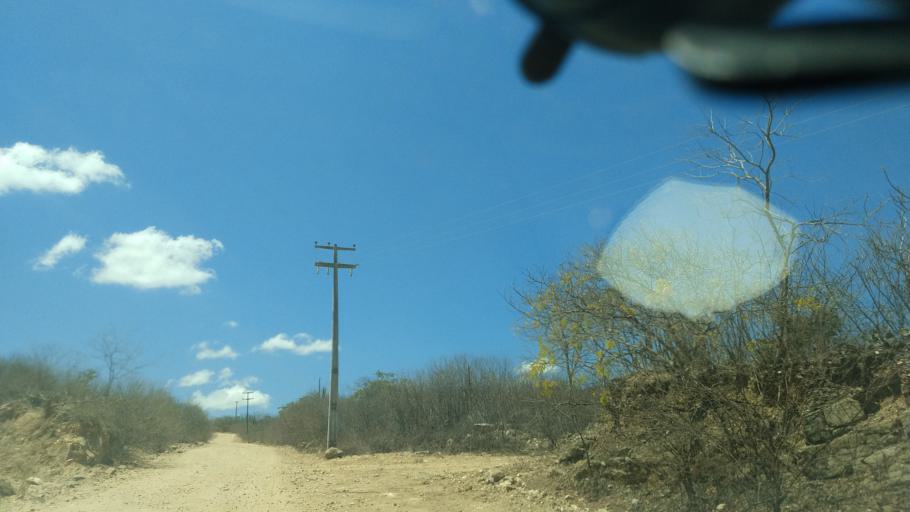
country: BR
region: Rio Grande do Norte
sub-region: Cerro Cora
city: Cerro Cora
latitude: -6.0114
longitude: -36.3234
